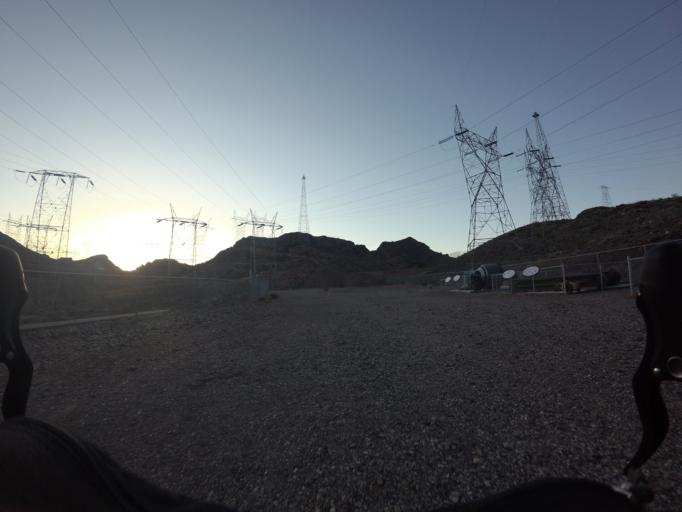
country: US
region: Nevada
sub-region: Clark County
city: Boulder City
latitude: 36.0177
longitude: -114.7438
